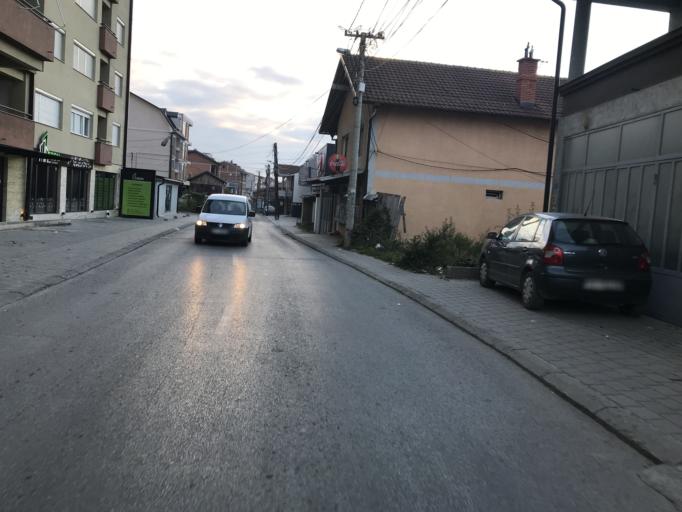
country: XK
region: Pec
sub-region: Komuna e Pejes
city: Peje
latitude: 42.6589
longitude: 20.2826
